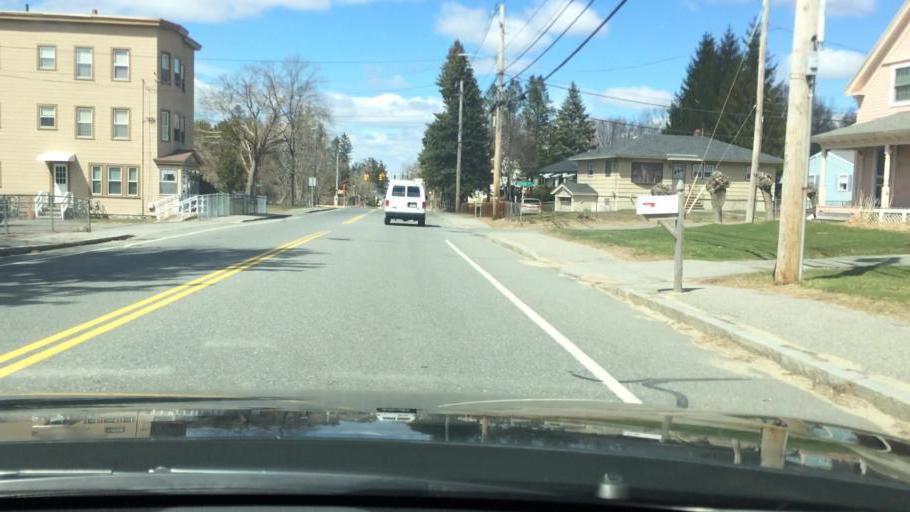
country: US
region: Massachusetts
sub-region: Essex County
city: Methuen
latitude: 42.7471
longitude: -71.1719
